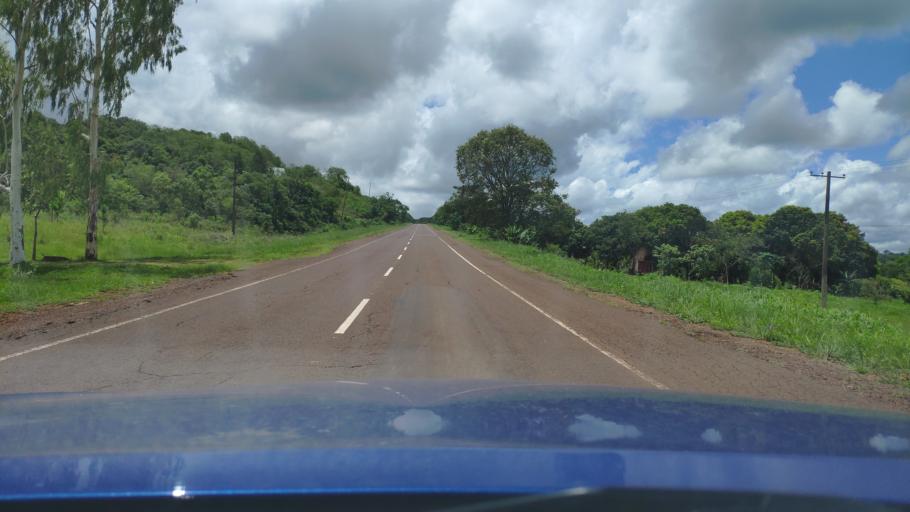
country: AR
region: Misiones
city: Dos Arroyos
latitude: -27.7605
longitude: -55.2491
